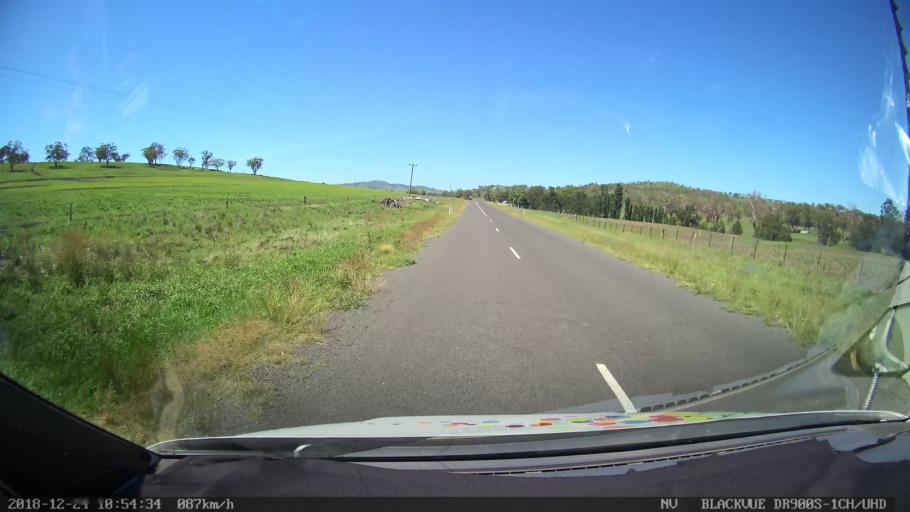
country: AU
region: New South Wales
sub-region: Upper Hunter Shire
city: Merriwa
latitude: -32.0060
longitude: 150.4174
